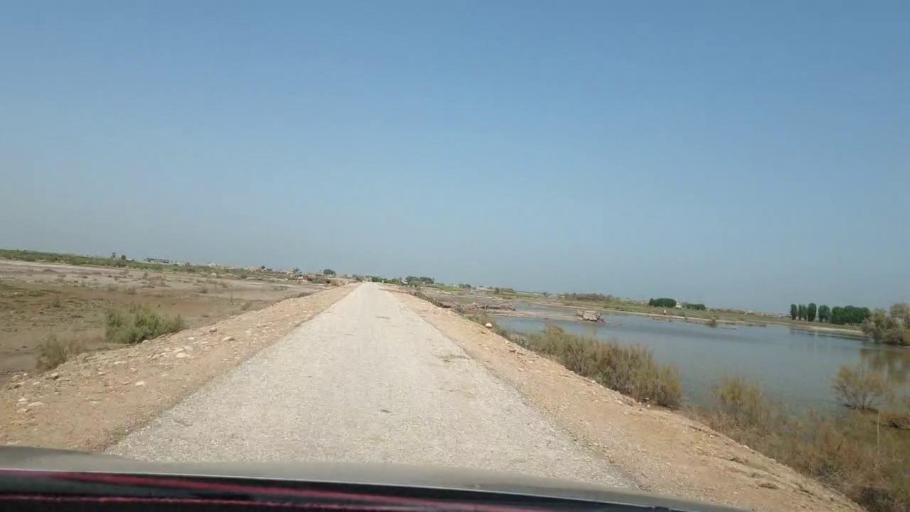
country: PK
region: Sindh
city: Warah
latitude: 27.5699
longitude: 67.7550
